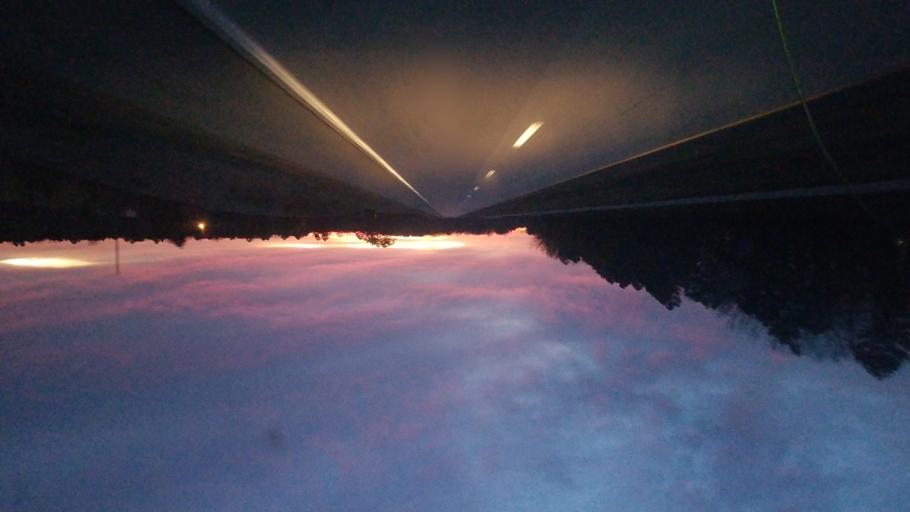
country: US
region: Missouri
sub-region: Shannon County
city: Winona
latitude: 36.9978
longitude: -91.4615
